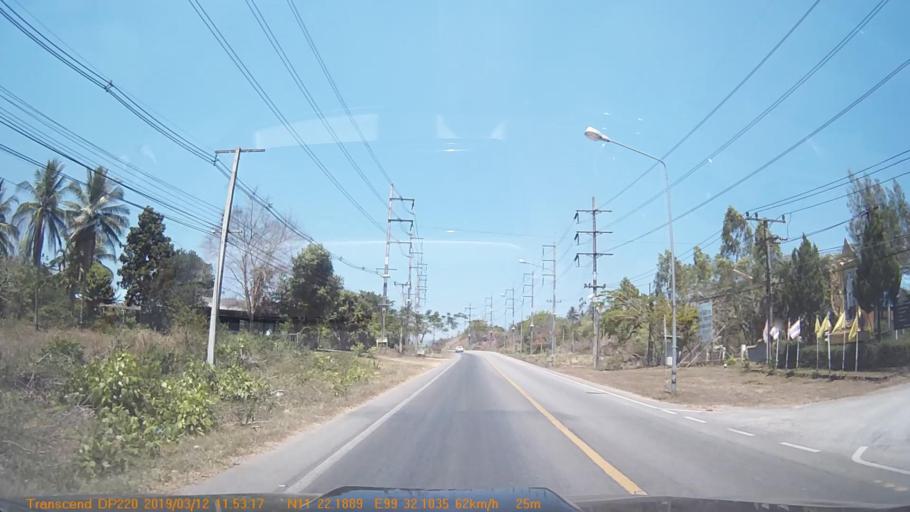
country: TH
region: Prachuap Khiri Khan
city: Thap Sakae
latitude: 11.3699
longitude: 99.5350
